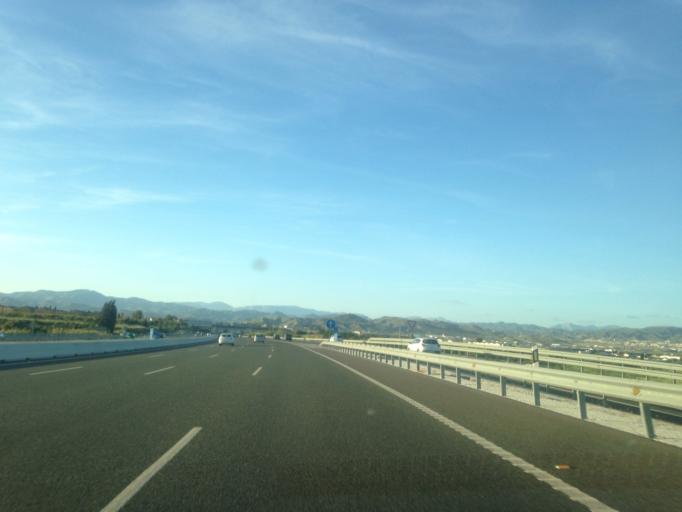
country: ES
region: Andalusia
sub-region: Provincia de Malaga
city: Alhaurin de la Torre
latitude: 36.6801
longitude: -4.5256
